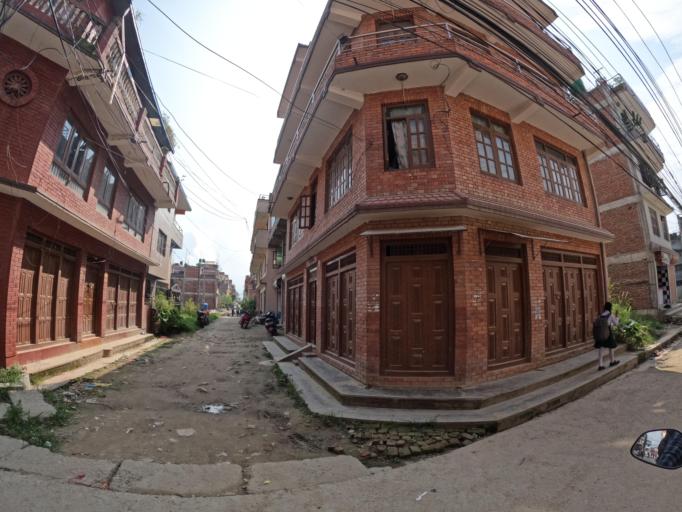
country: NP
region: Central Region
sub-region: Bagmati Zone
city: Bhaktapur
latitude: 27.6780
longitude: 85.4424
